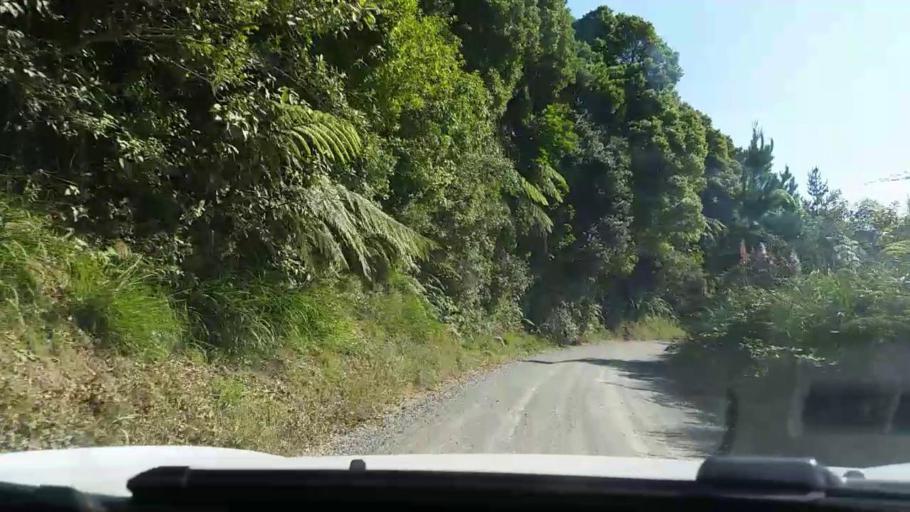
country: NZ
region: Bay of Plenty
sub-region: Western Bay of Plenty District
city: Maketu
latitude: -37.9602
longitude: 176.4375
